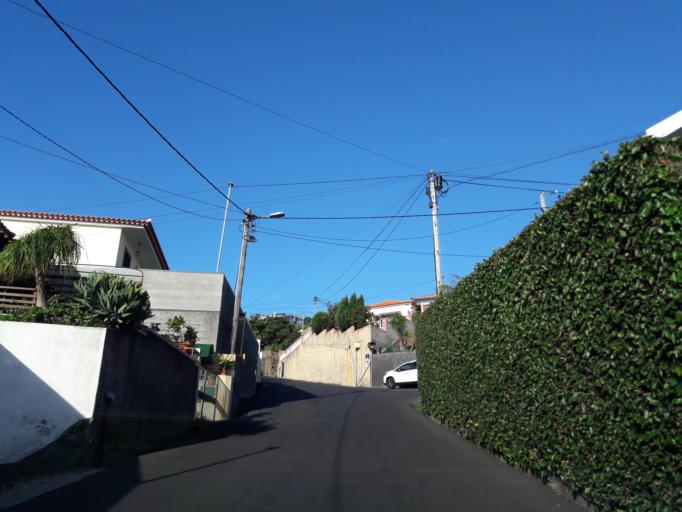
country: PT
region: Madeira
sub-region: Funchal
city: Nossa Senhora do Monte
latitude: 32.6719
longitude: -16.9211
